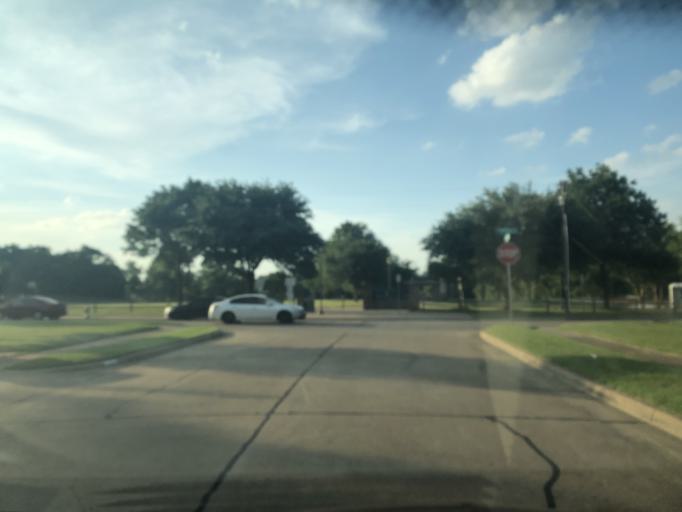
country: US
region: Texas
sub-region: Dallas County
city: Irving
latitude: 32.7967
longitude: -96.9553
